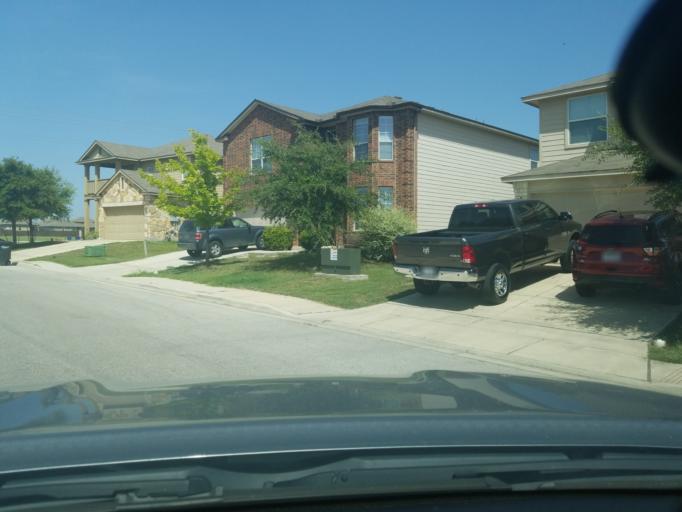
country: US
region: Texas
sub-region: Guadalupe County
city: Lake Dunlap
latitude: 29.6716
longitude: -98.0397
